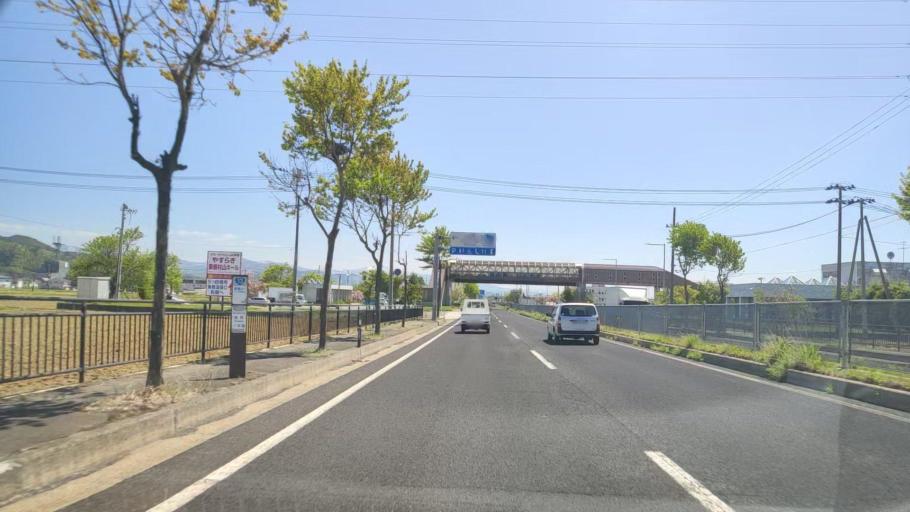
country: JP
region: Yamagata
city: Higashine
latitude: 38.4884
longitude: 140.3831
